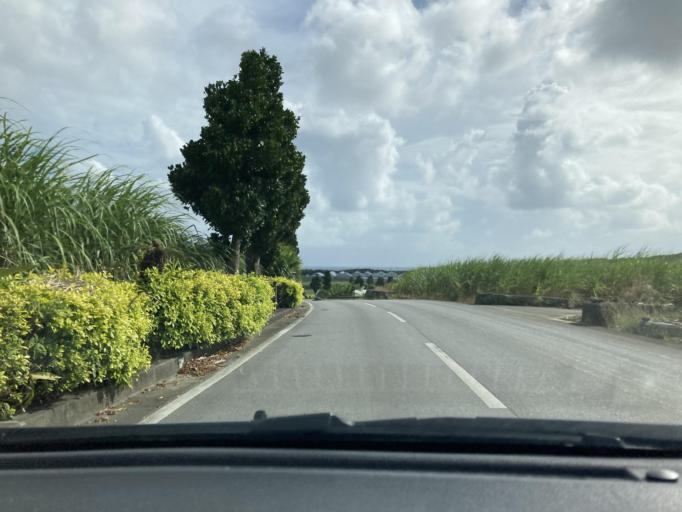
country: JP
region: Okinawa
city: Itoman
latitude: 26.0922
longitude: 127.6940
